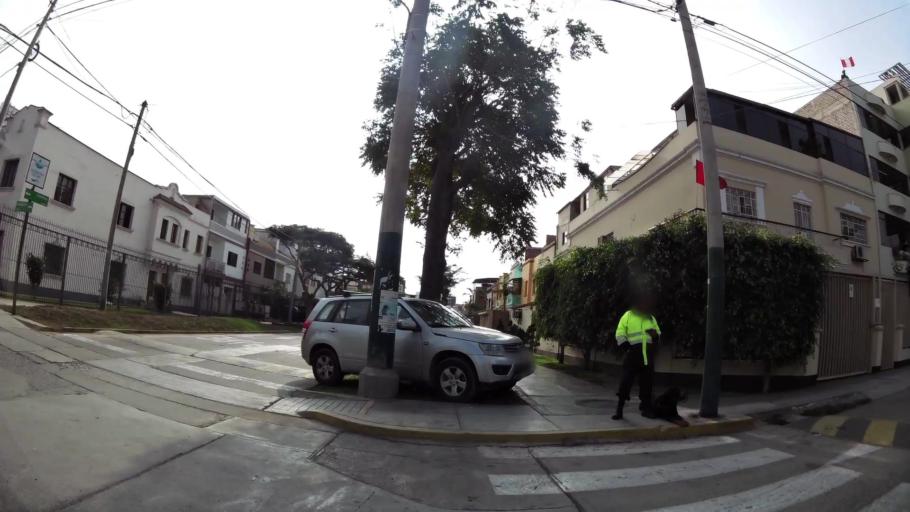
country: PE
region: Lima
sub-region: Lima
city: San Isidro
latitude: -12.0901
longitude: -77.0633
